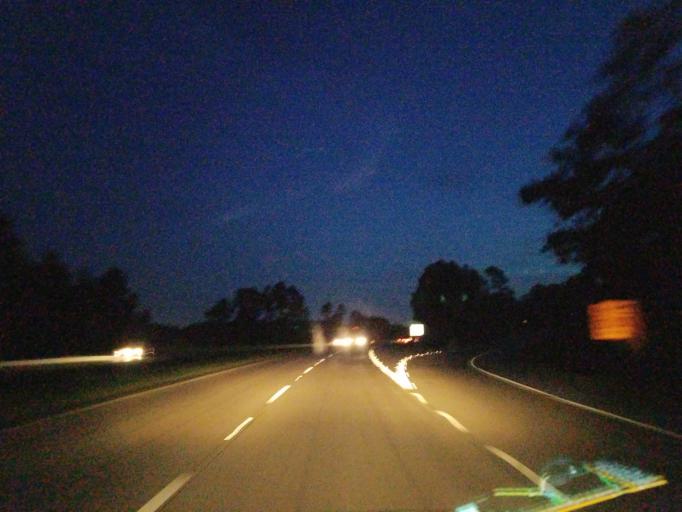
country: US
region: Mississippi
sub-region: Forrest County
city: Glendale
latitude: 31.3835
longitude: -89.3223
